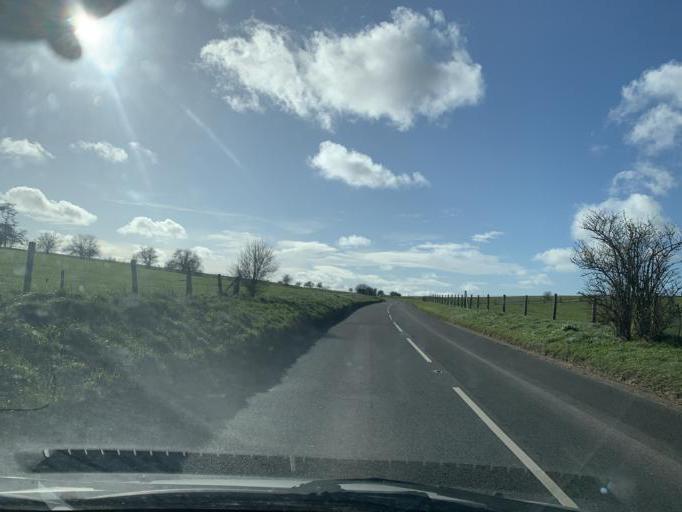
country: GB
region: England
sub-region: Wiltshire
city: Shrewton
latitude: 51.1940
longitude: -1.9423
